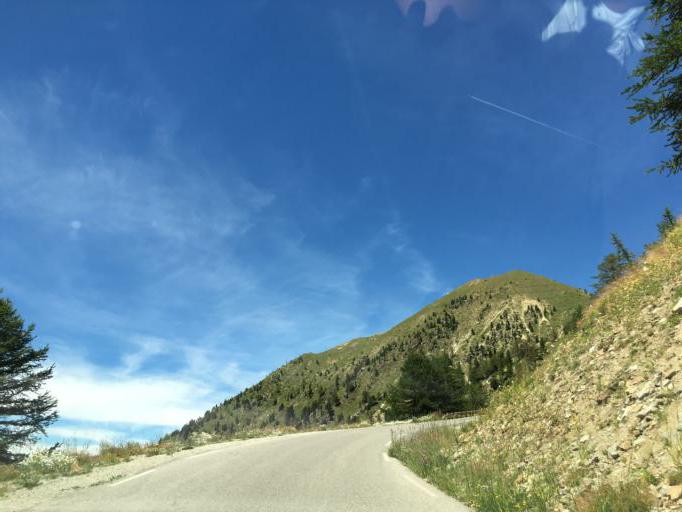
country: IT
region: Piedmont
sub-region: Provincia di Cuneo
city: Vinadio
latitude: 44.1926
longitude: 7.1557
